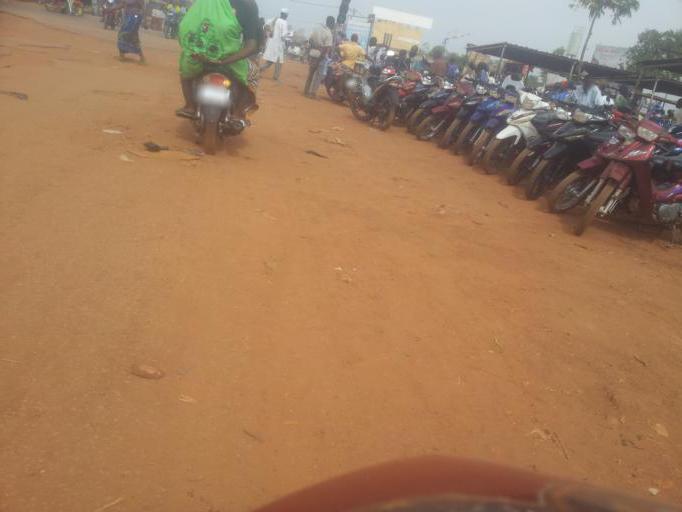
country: BF
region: Centre
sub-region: Kadiogo Province
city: Ouagadougou
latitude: 12.3831
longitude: -1.5523
